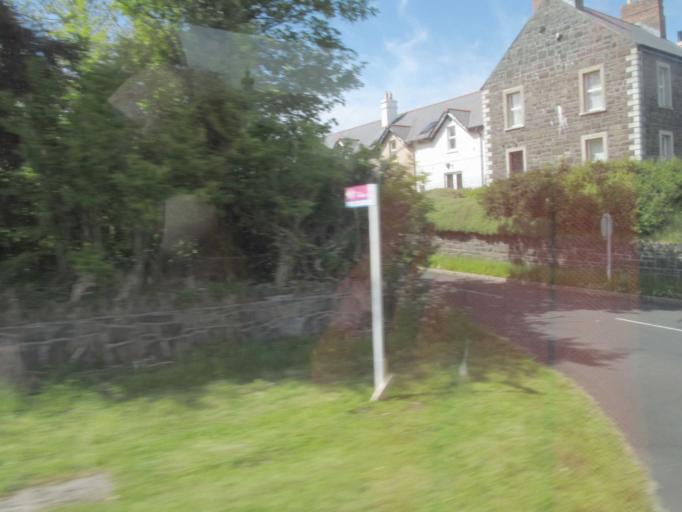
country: GB
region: Northern Ireland
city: Bushmills
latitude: 55.2008
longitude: -6.5276
